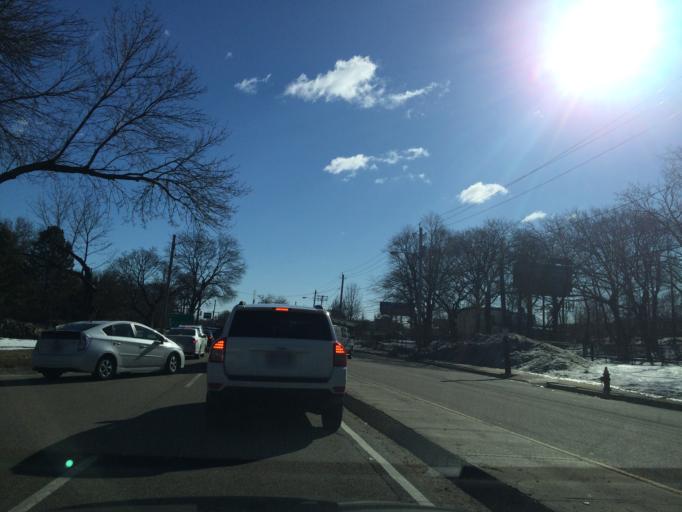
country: US
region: Massachusetts
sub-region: Middlesex County
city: Watertown
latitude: 42.3586
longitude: -71.1604
